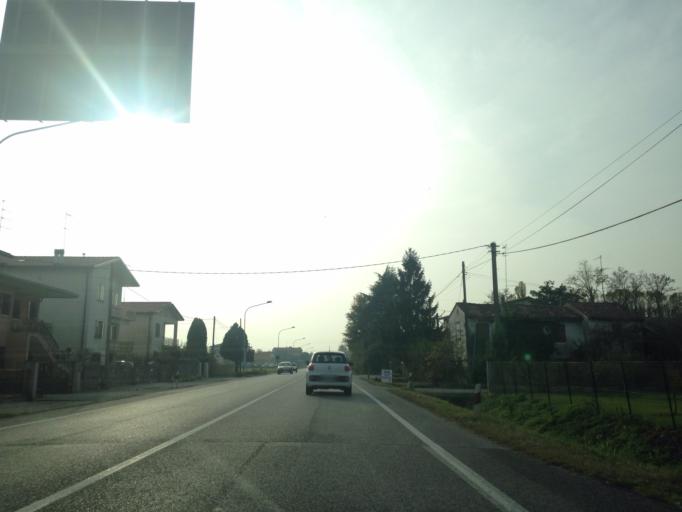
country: IT
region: Veneto
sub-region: Provincia di Treviso
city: Oderzo
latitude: 45.7951
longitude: 12.5108
